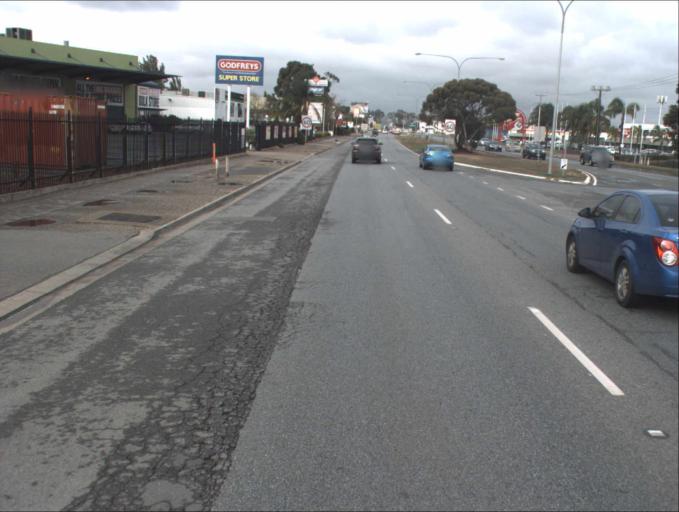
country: AU
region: South Australia
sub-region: Port Adelaide Enfield
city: Enfield
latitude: -34.8439
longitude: 138.6000
